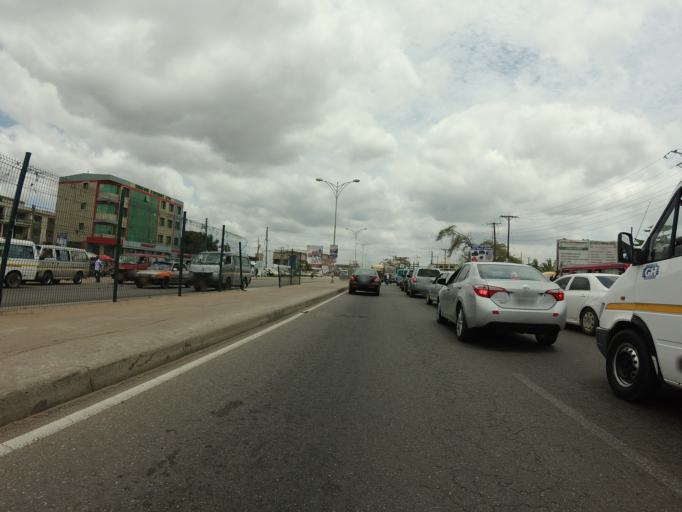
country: GH
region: Greater Accra
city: Gbawe
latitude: 5.5735
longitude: -0.2792
